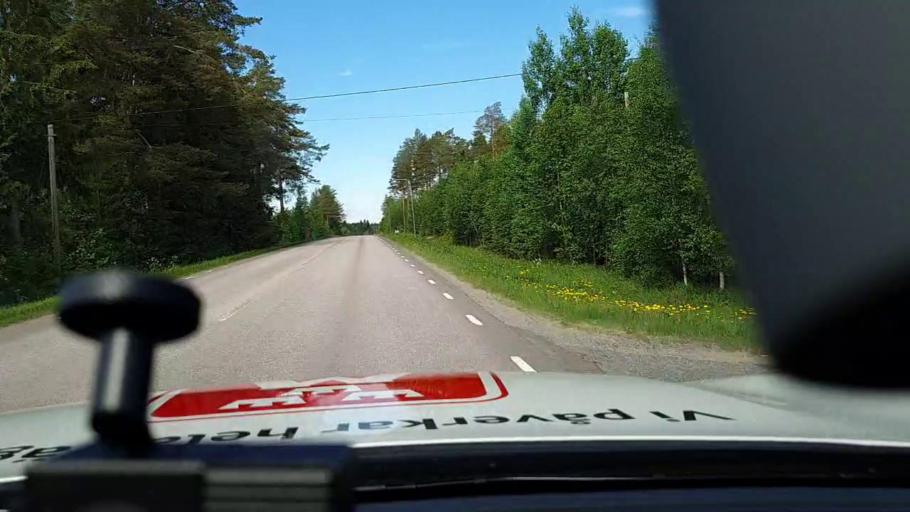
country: SE
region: Norrbotten
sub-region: Lulea Kommun
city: Sodra Sunderbyn
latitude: 65.6411
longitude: 21.8989
